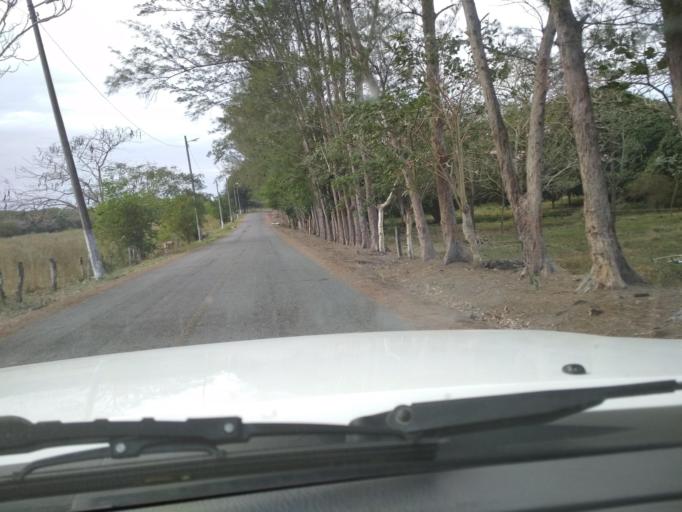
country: MX
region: Veracruz
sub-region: Veracruz
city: Delfino Victoria (Santa Fe)
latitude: 19.1561
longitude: -96.2931
